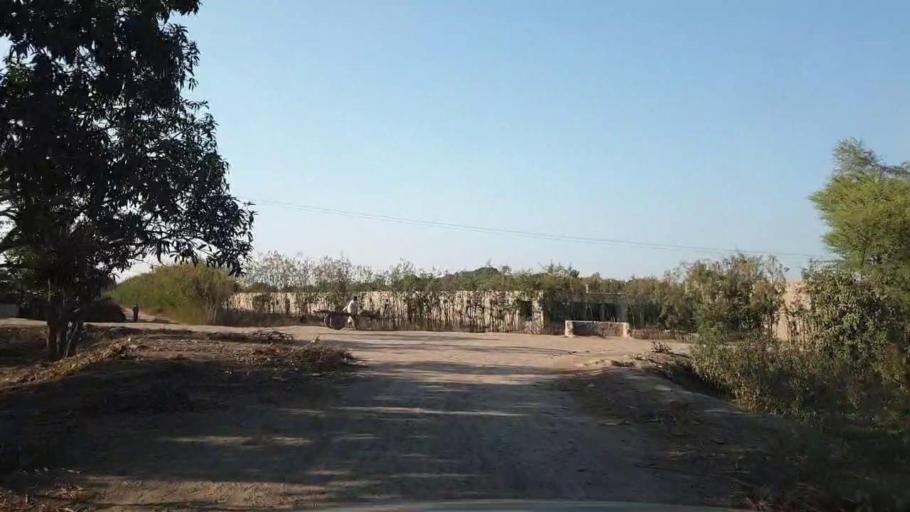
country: PK
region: Sindh
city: Tando Allahyar
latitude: 25.4883
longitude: 68.6405
